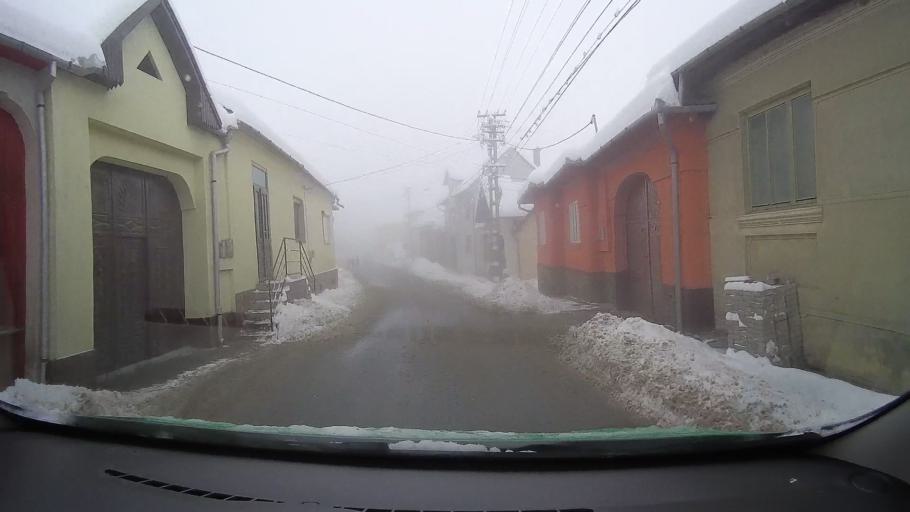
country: RO
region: Sibiu
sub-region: Comuna Jina
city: Jina
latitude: 45.7845
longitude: 23.6789
